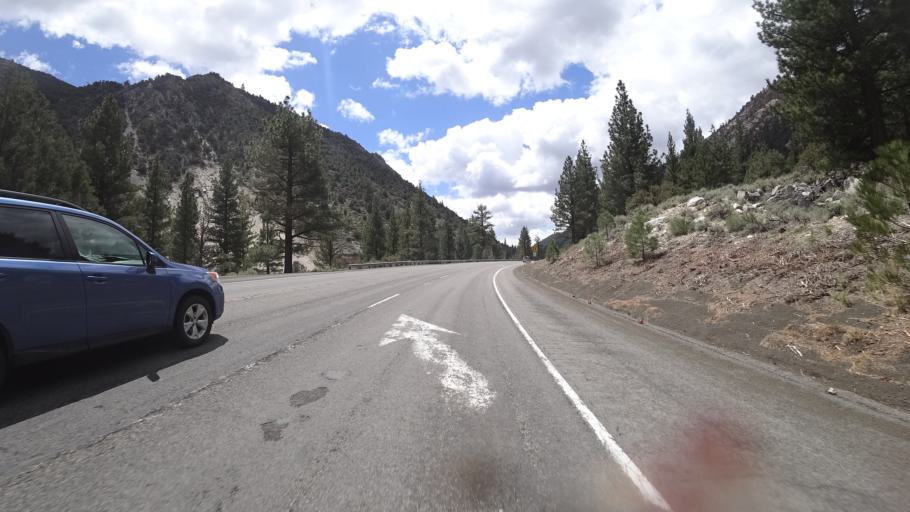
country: US
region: California
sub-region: Mono County
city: Bridgeport
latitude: 38.4208
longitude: -119.4475
